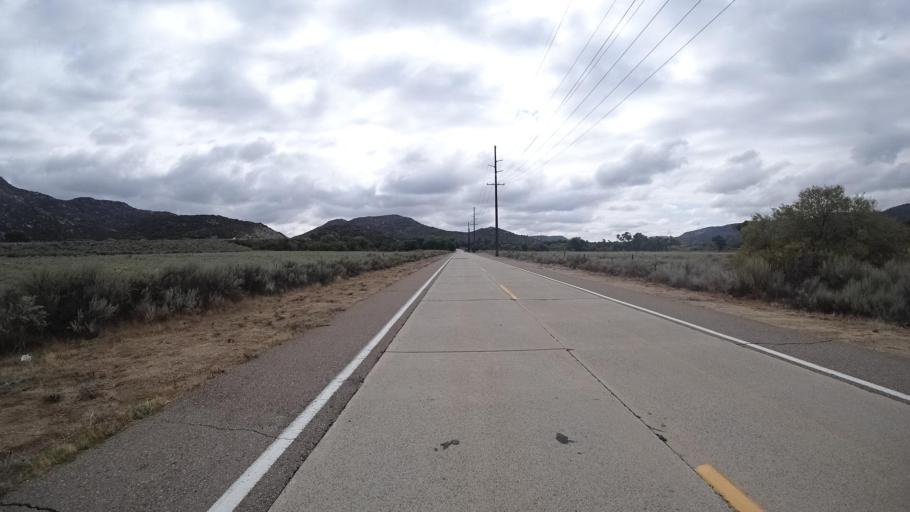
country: US
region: California
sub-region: San Diego County
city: Pine Valley
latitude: 32.7380
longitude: -116.4821
